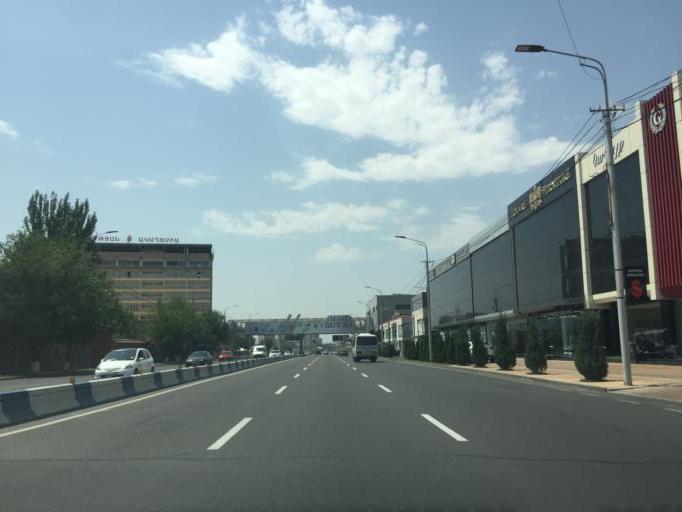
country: AM
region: Ararat
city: Argavand
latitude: 40.1578
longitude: 44.4501
